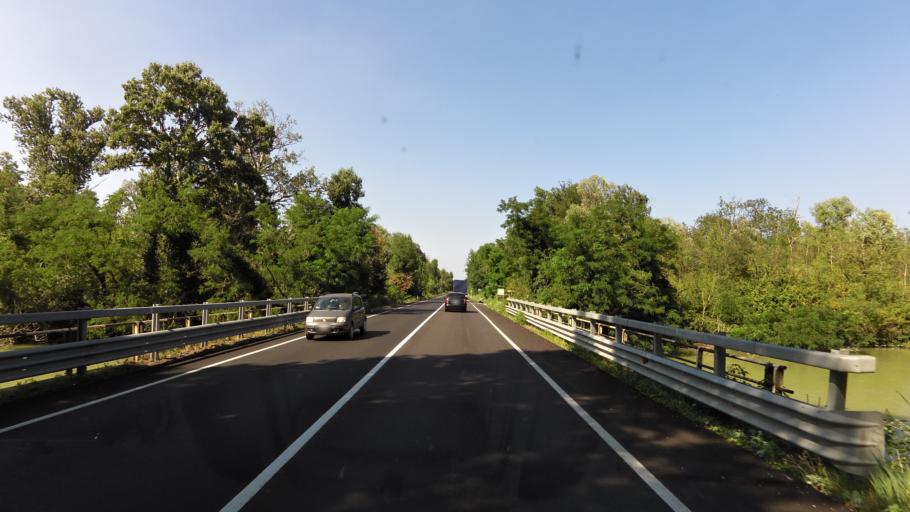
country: IT
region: Emilia-Romagna
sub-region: Provincia di Ravenna
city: Marina Romea
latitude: 44.5074
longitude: 12.2225
